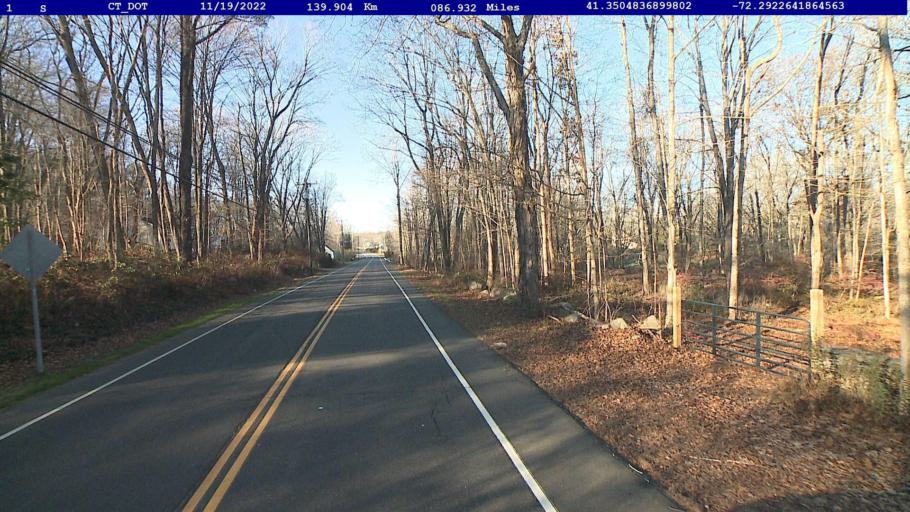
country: US
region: Connecticut
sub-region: Middlesex County
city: Old Saybrook Center
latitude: 41.3505
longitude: -72.2923
